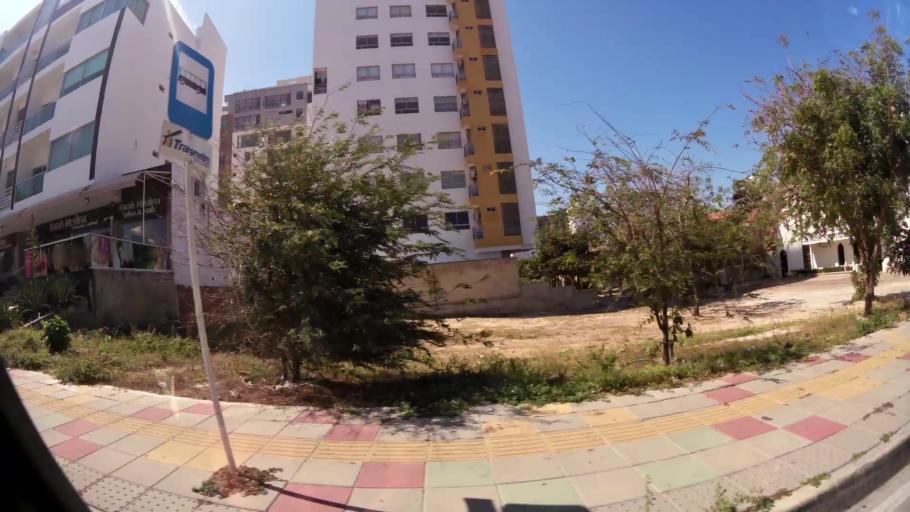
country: CO
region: Atlantico
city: Barranquilla
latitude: 11.0132
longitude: -74.8344
